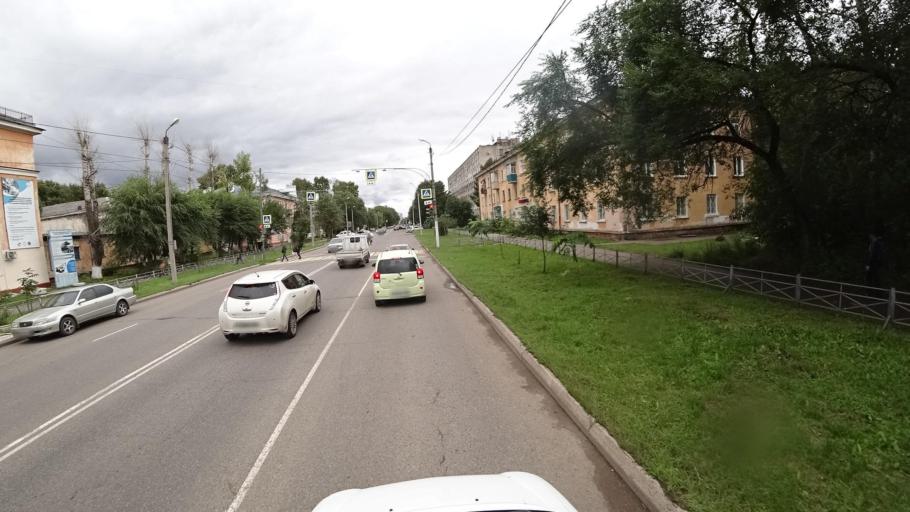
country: RU
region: Khabarovsk Krai
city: Komsomolsk-on-Amur
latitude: 50.5503
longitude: 137.0276
